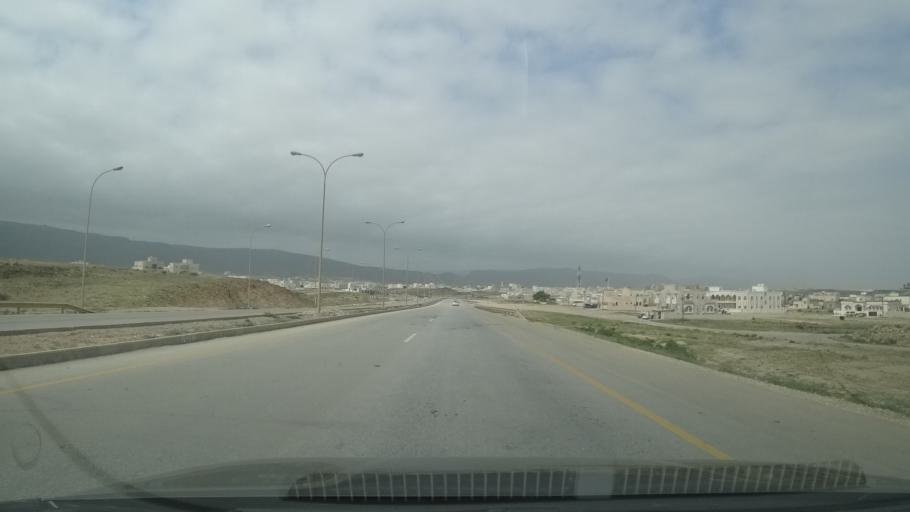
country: OM
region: Zufar
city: Salalah
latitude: 17.0474
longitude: 54.3831
